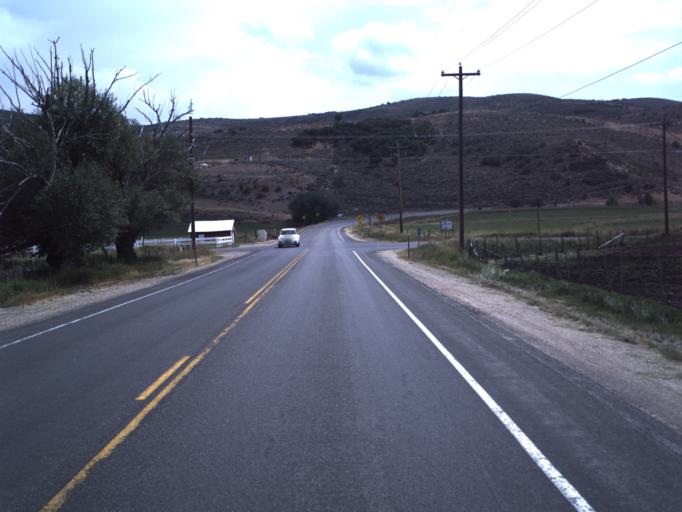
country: US
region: Utah
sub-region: Summit County
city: Francis
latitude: 40.6106
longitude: -111.2626
